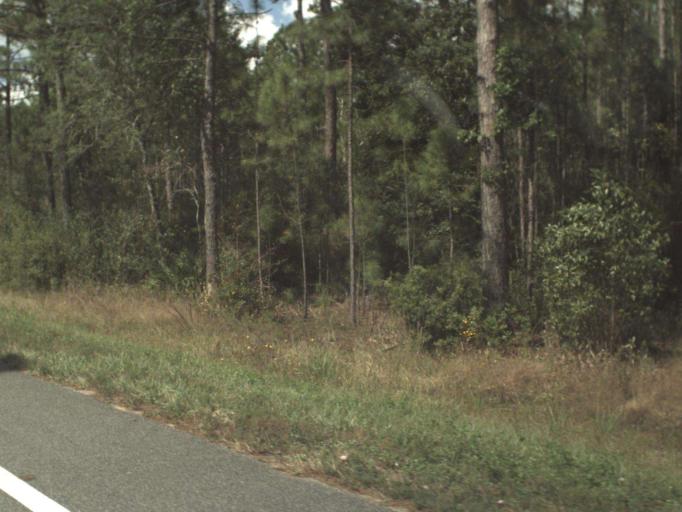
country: US
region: Florida
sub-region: Walton County
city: Freeport
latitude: 30.4763
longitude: -86.0274
